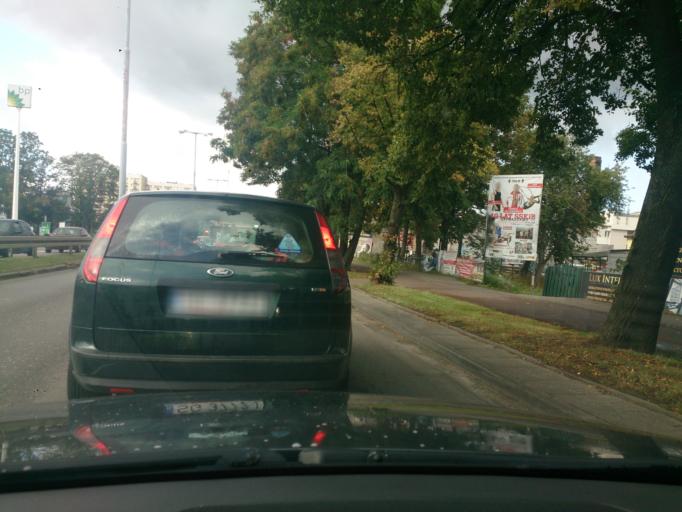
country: PL
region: Pomeranian Voivodeship
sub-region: Sopot
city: Sopot
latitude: 54.4290
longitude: 18.5624
